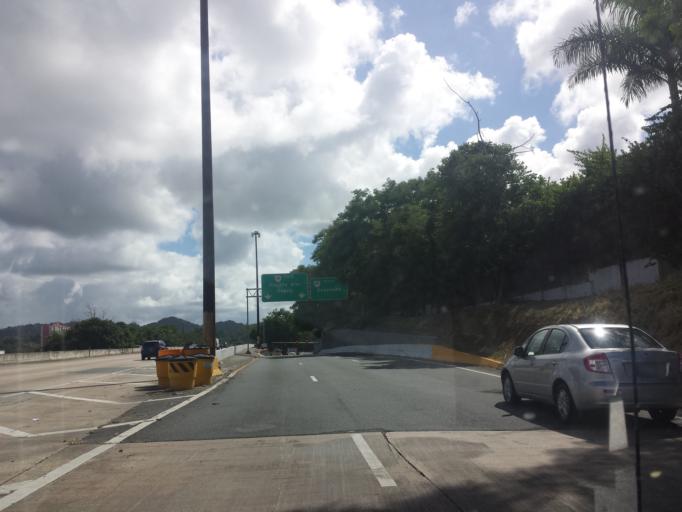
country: PR
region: Guaynabo
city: Guaynabo
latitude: 18.3605
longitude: -66.0705
